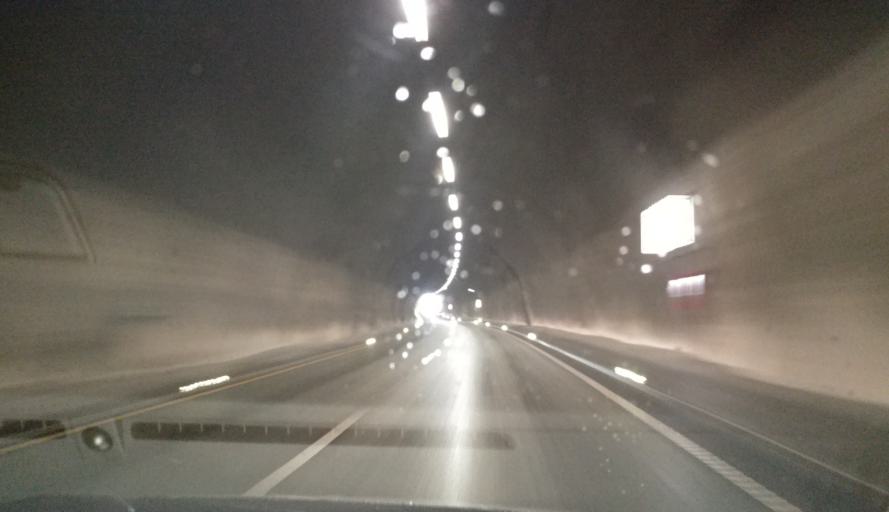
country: NO
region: Sor-Trondelag
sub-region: Trondheim
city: Trondheim
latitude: 63.4286
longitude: 10.5042
